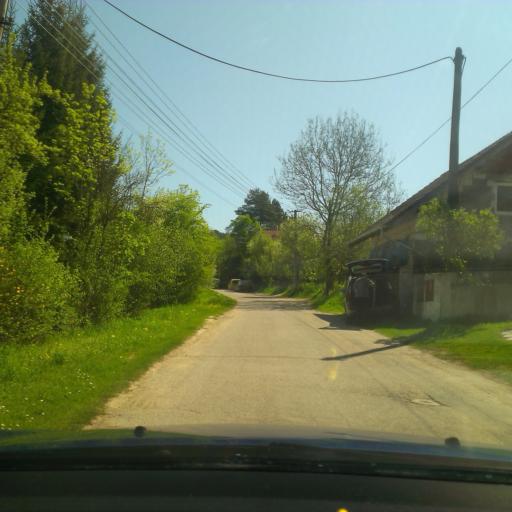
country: SK
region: Trnavsky
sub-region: Okres Trnava
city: Piestany
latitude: 48.6613
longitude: 17.8898
